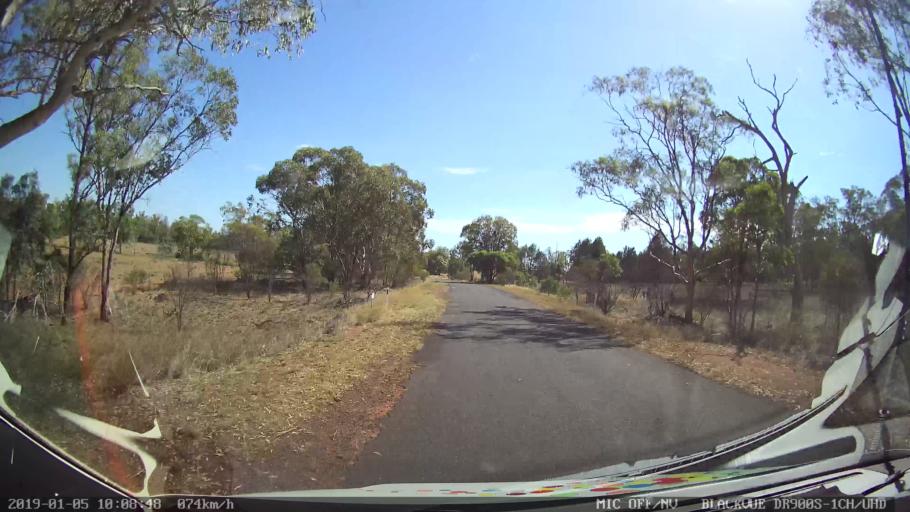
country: AU
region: New South Wales
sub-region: Gilgandra
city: Gilgandra
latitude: -31.6375
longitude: 148.8823
